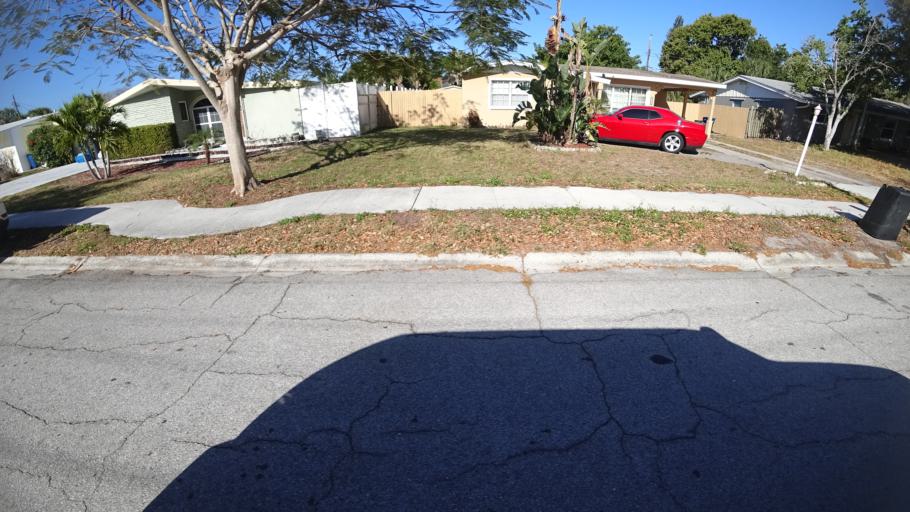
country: US
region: Florida
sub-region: Manatee County
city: Bayshore Gardens
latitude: 27.4216
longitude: -82.5901
